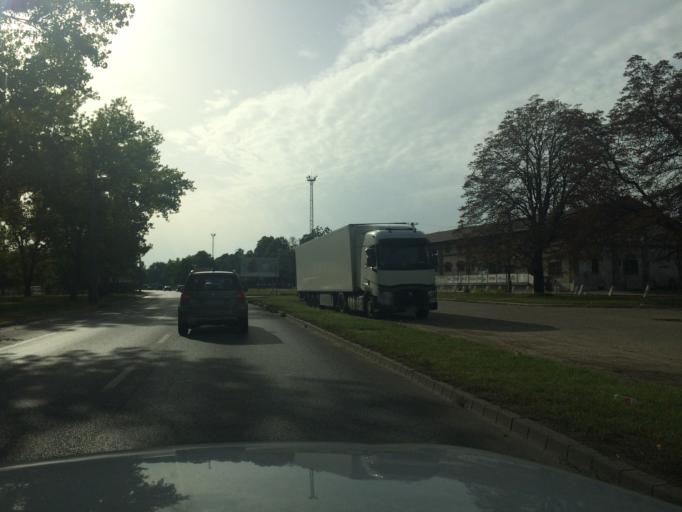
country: HU
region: Szabolcs-Szatmar-Bereg
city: Nyiregyhaza
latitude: 47.9450
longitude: 21.7073
